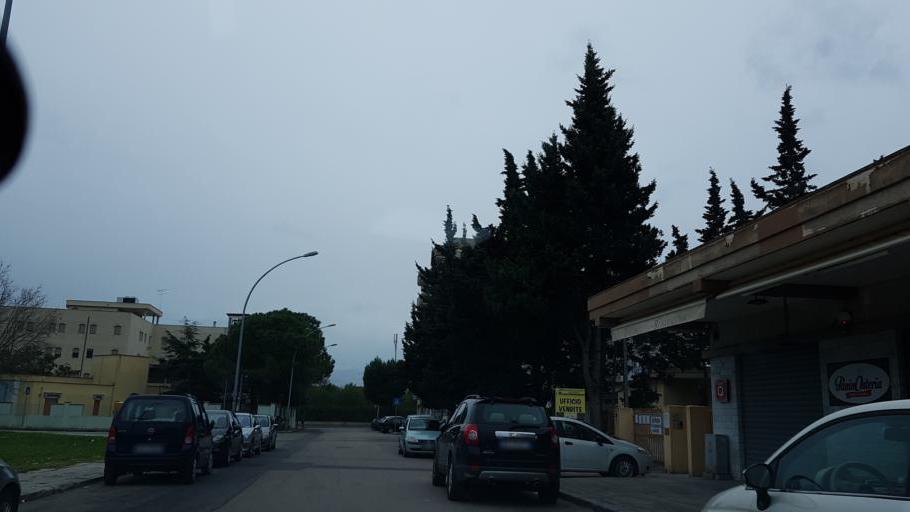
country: IT
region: Apulia
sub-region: Provincia di Brindisi
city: Brindisi
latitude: 40.6247
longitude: 17.9235
